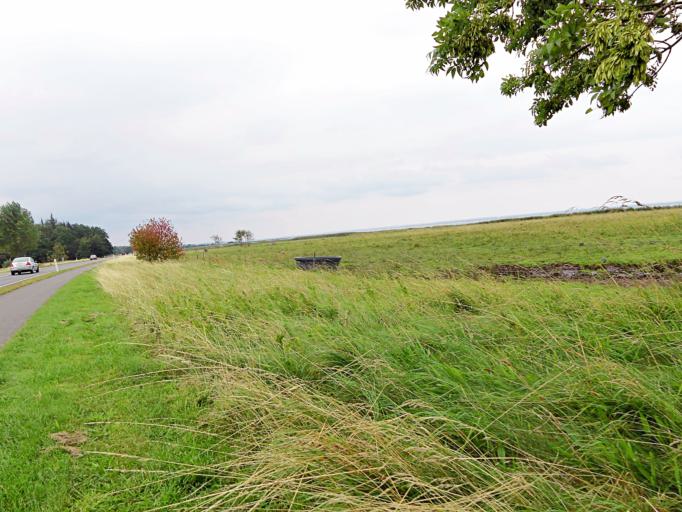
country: DK
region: Capital Region
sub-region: Fredensborg Kommune
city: Kokkedal
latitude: 55.9198
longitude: 12.5150
